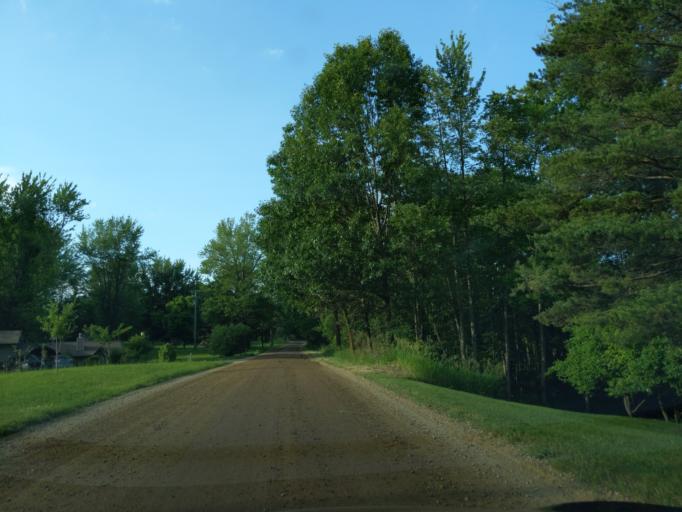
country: US
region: Michigan
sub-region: Shiawassee County
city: Laingsburg
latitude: 42.8548
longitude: -84.3634
